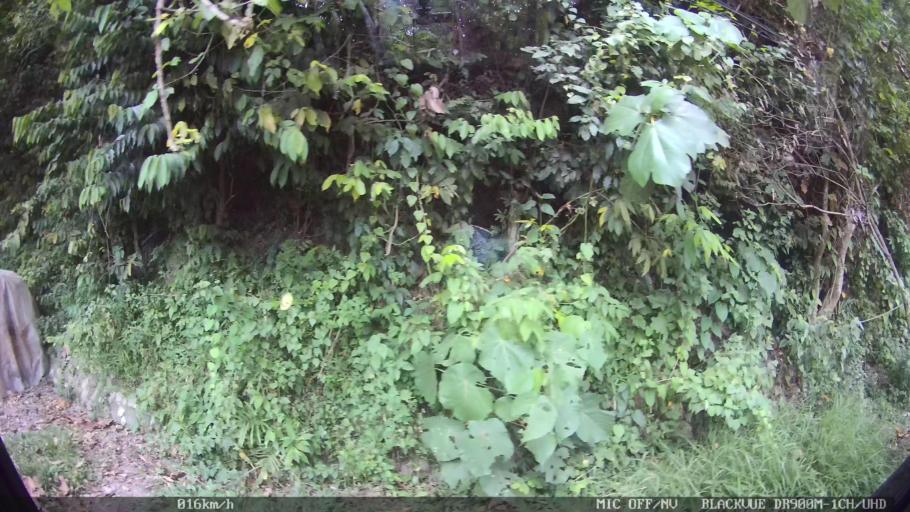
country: ID
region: Lampung
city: Panjang
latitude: -5.4390
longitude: 105.3150
